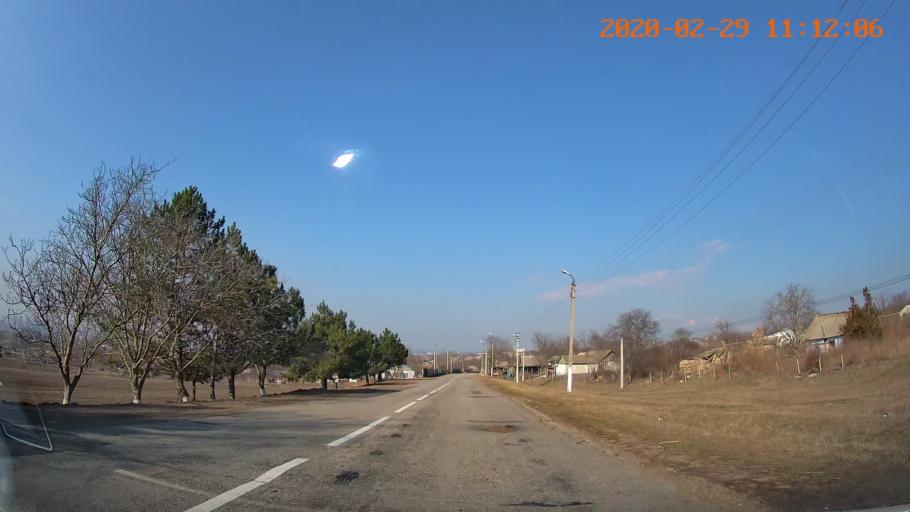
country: MD
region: Telenesti
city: Dubasari
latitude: 47.2599
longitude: 29.1889
